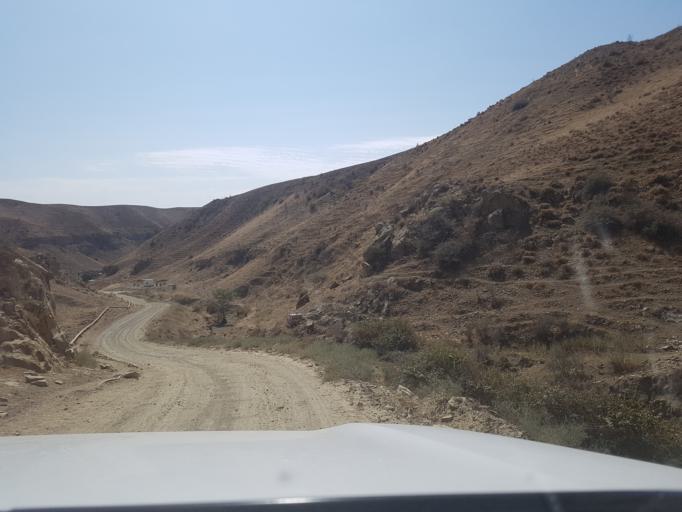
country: TM
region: Ahal
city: Baharly
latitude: 38.2389
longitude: 56.8921
